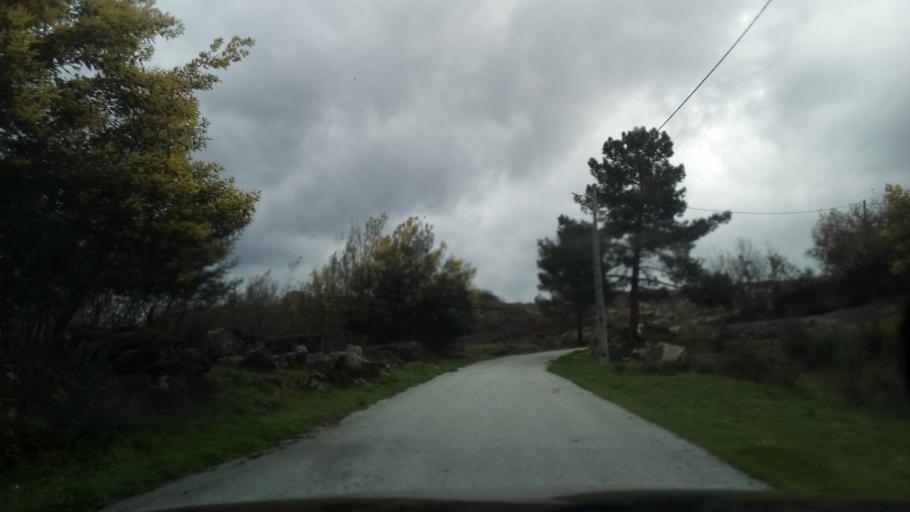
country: PT
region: Guarda
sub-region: Fornos de Algodres
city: Fornos de Algodres
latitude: 40.5863
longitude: -7.5678
